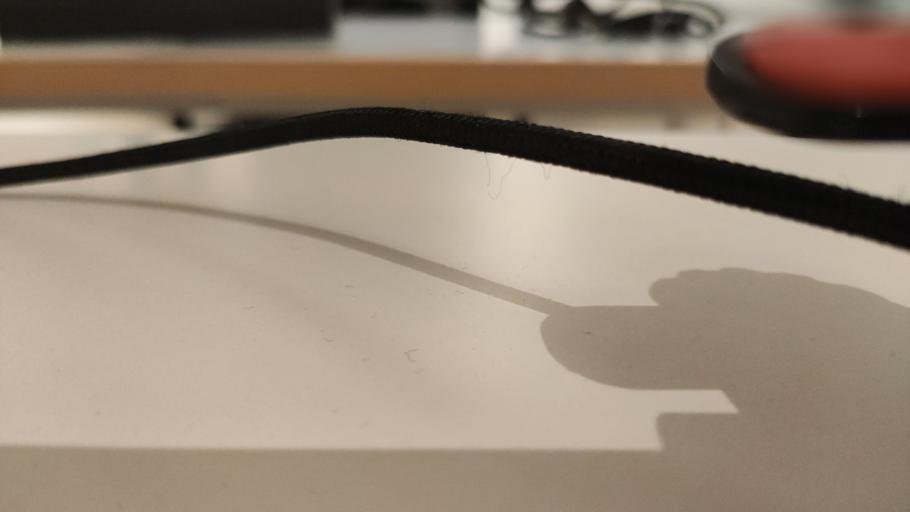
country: RU
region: Moskovskaya
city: Dorokhovo
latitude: 55.5250
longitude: 36.3545
